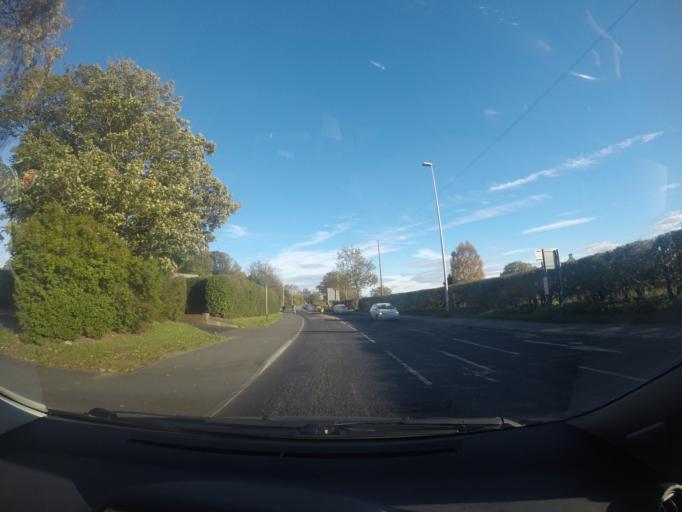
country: GB
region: England
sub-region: City of York
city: Nether Poppleton
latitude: 53.9722
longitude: -1.1418
